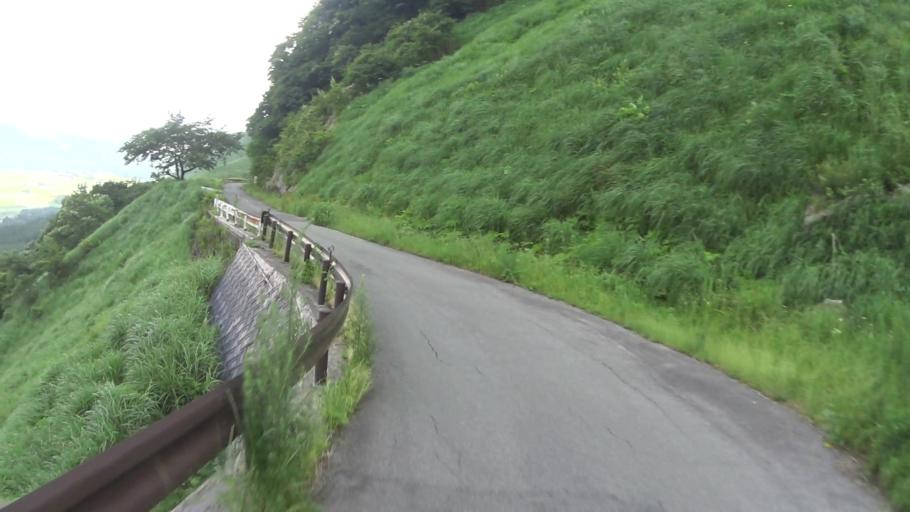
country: JP
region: Kumamoto
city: Aso
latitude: 32.9608
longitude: 130.9996
